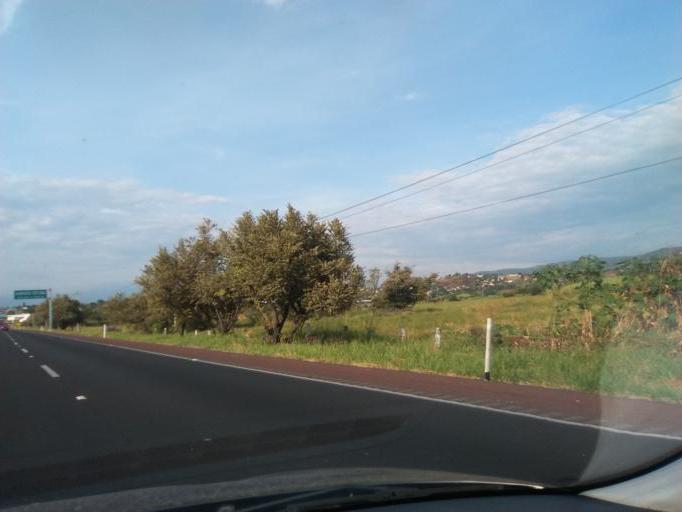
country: MX
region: Morelos
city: Xochitepec
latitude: 18.7961
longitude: -99.2209
